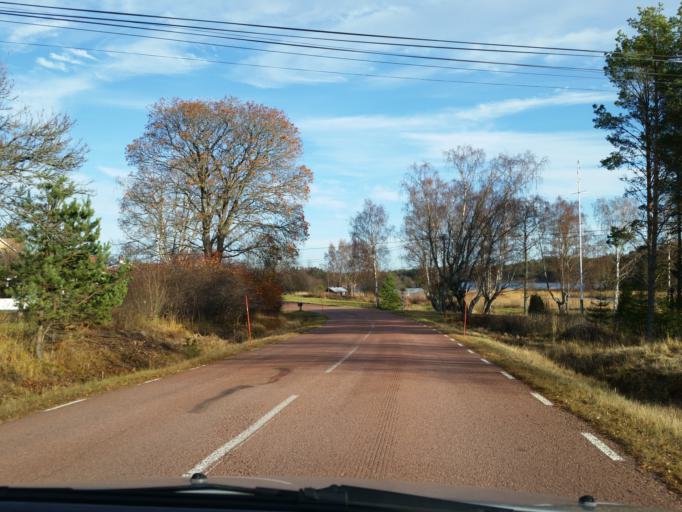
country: AX
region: Alands landsbygd
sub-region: Saltvik
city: Saltvik
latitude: 60.3464
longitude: 20.0909
